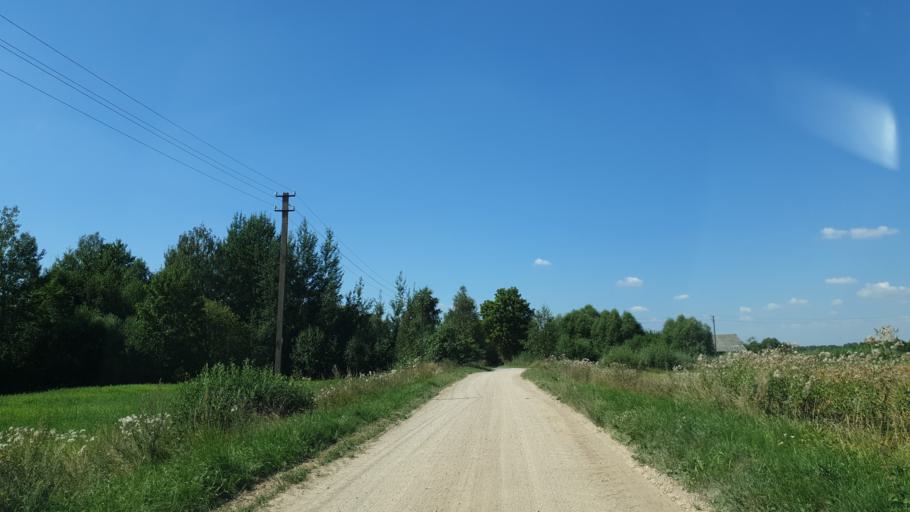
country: LT
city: Sirvintos
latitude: 54.9161
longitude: 24.9171
